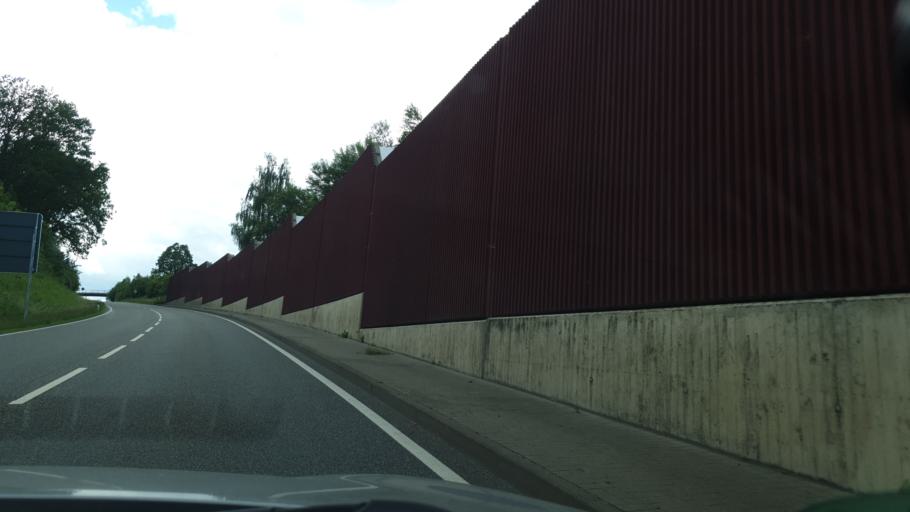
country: DE
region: Rheinland-Pfalz
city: Hohr-Grenzhausen
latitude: 50.4304
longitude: 7.6839
